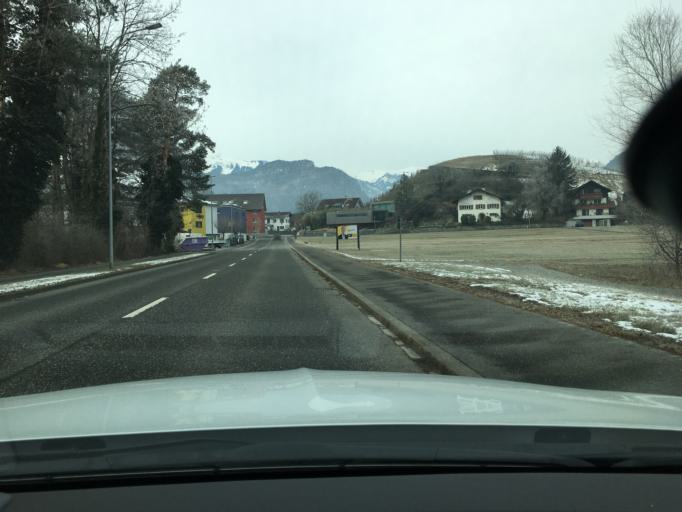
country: LI
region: Balzers
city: Balzers
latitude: 47.0633
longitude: 9.5022
